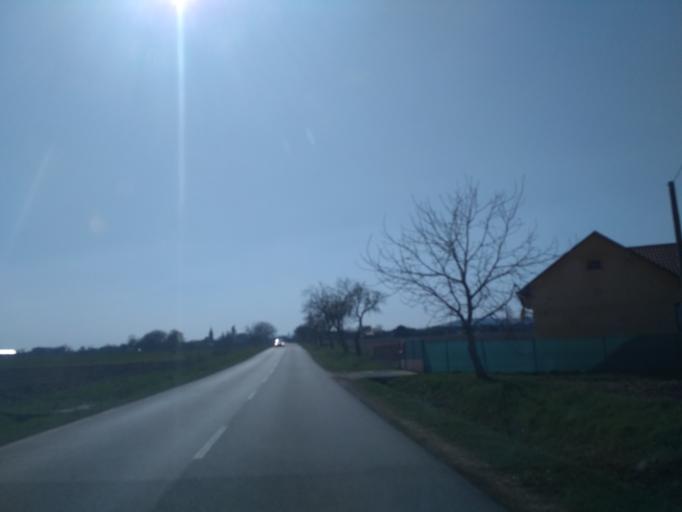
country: SK
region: Kosicky
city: Secovce
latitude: 48.6864
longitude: 21.6230
